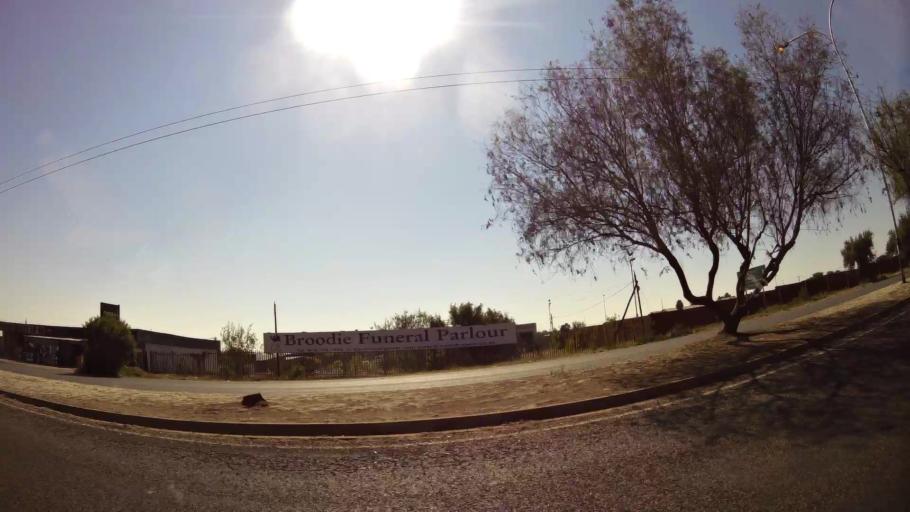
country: ZA
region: Gauteng
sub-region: City of Tshwane Metropolitan Municipality
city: Mabopane
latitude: -25.5228
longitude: 28.0972
